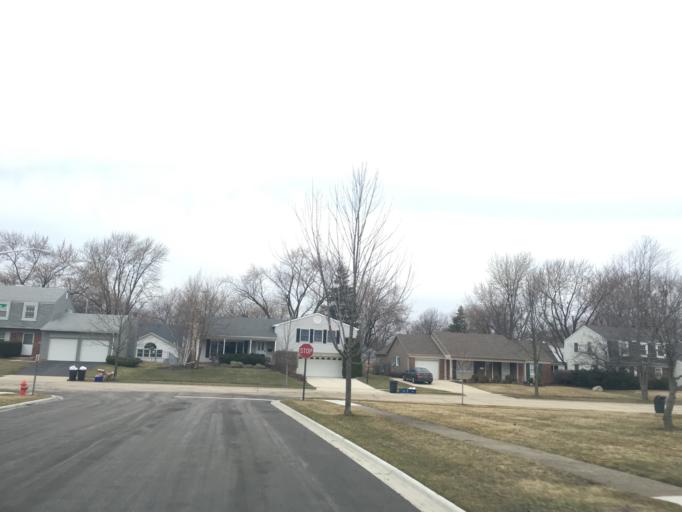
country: US
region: Illinois
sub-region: DuPage County
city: Hanover Park
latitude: 42.0288
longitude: -88.1240
